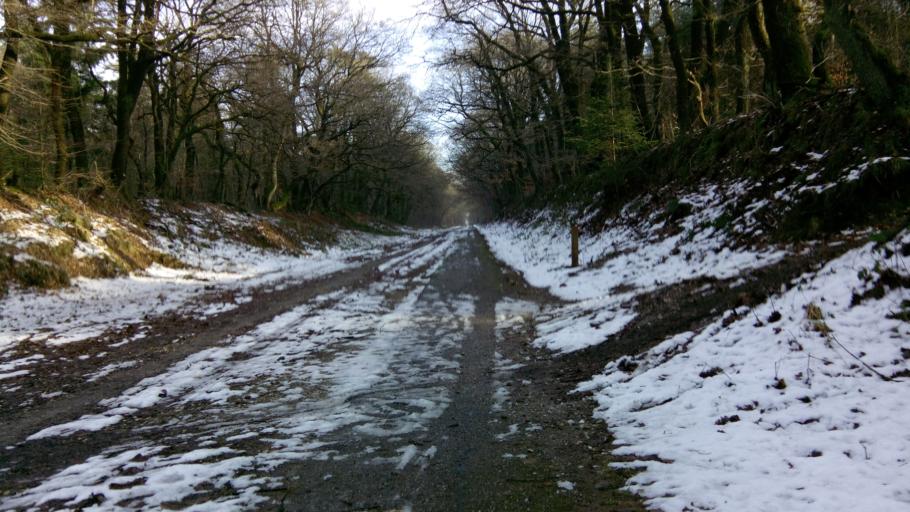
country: NL
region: Gelderland
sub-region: Gemeente Groesbeek
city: Berg en Dal
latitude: 51.7862
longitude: 5.8961
